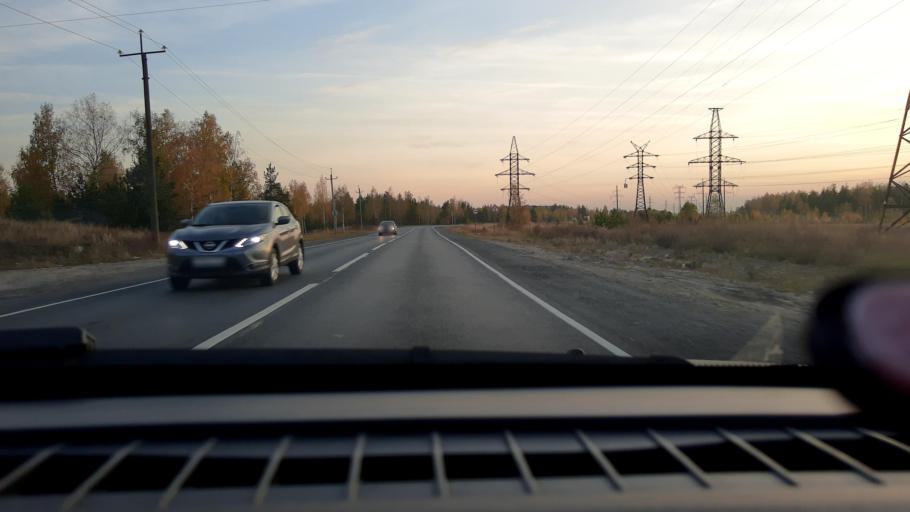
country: RU
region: Nizjnij Novgorod
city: Lukino
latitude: 56.3389
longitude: 43.5788
